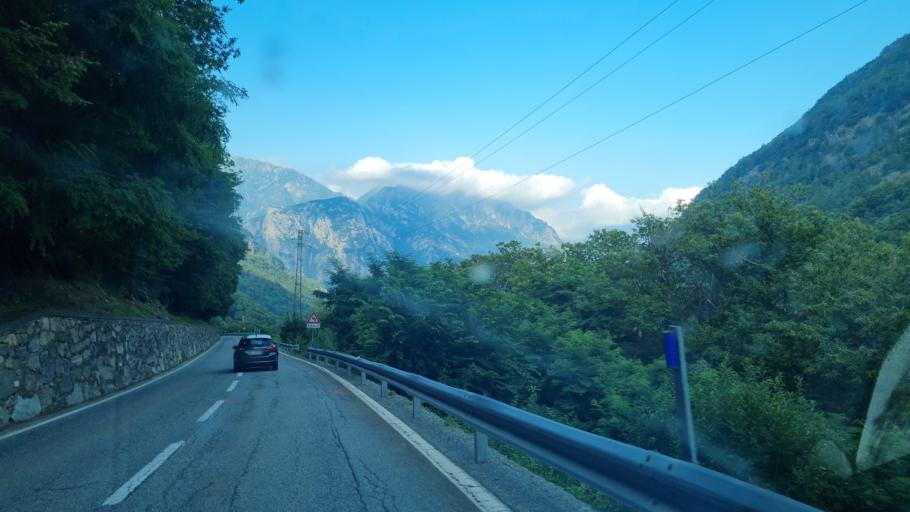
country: IT
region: Aosta Valley
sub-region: Valle d'Aosta
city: Pont-Bozet
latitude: 45.6067
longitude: 7.6987
